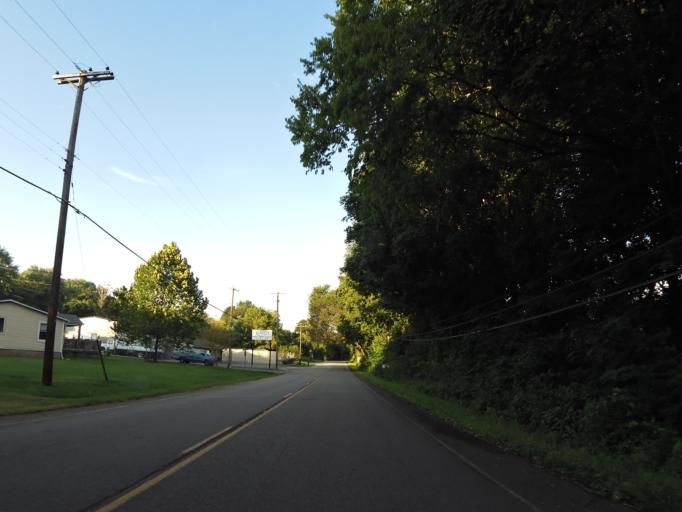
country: US
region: Tennessee
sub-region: Knox County
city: Mascot
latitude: 36.0372
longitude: -83.8190
